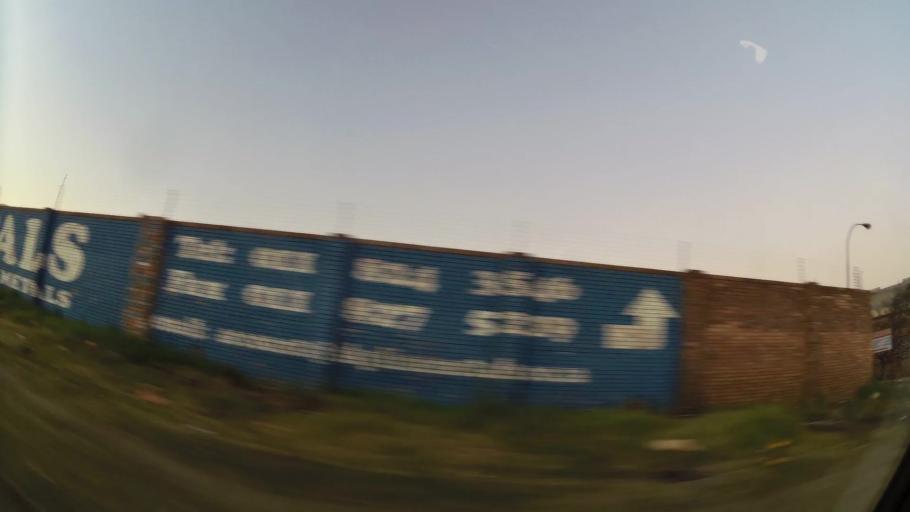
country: ZA
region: Gauteng
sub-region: Ekurhuleni Metropolitan Municipality
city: Germiston
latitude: -26.2664
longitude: 28.1715
